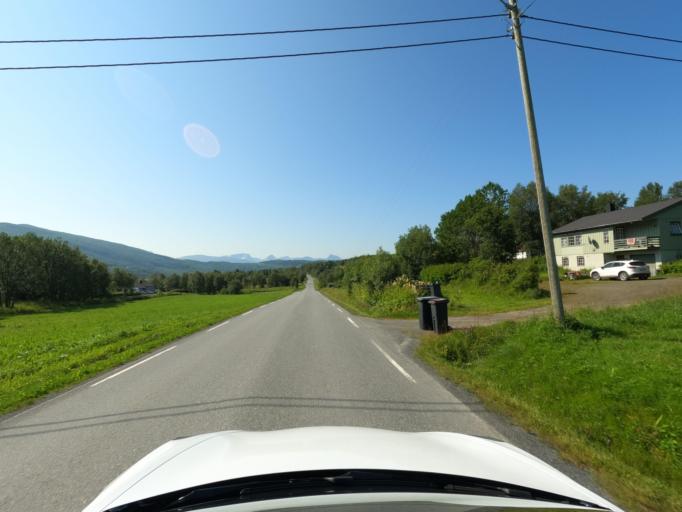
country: NO
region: Nordland
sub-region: Ballangen
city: Ballangen
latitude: 68.3500
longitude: 16.8569
